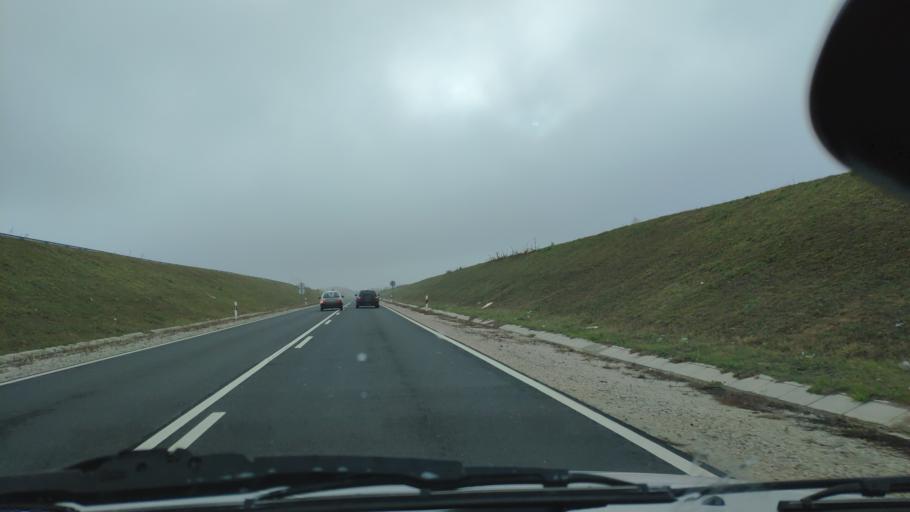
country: HU
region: Zala
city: Nagykanizsa
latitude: 46.4599
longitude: 17.0358
